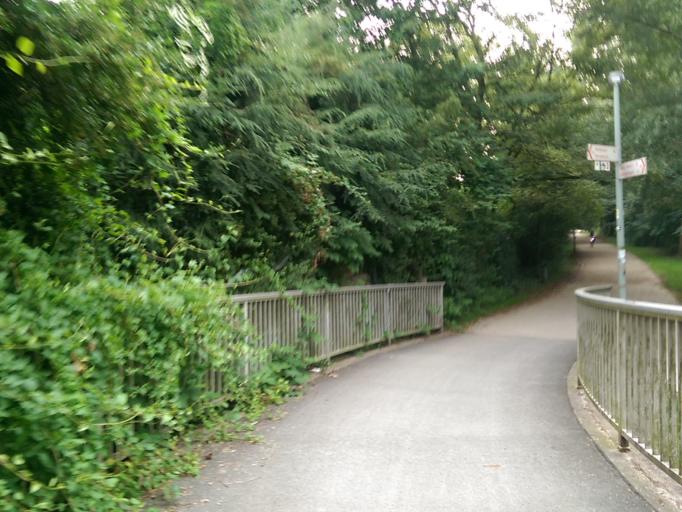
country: DE
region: North Rhine-Westphalia
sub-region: Regierungsbezirk Detmold
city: Guetersloh
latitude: 51.9012
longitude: 8.3616
